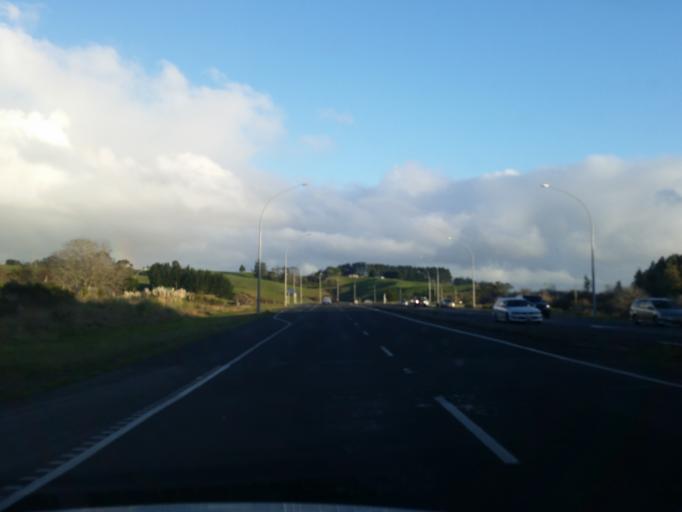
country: NZ
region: Waikato
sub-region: Waikato District
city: Te Kauwhata
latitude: -37.3241
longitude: 175.0663
